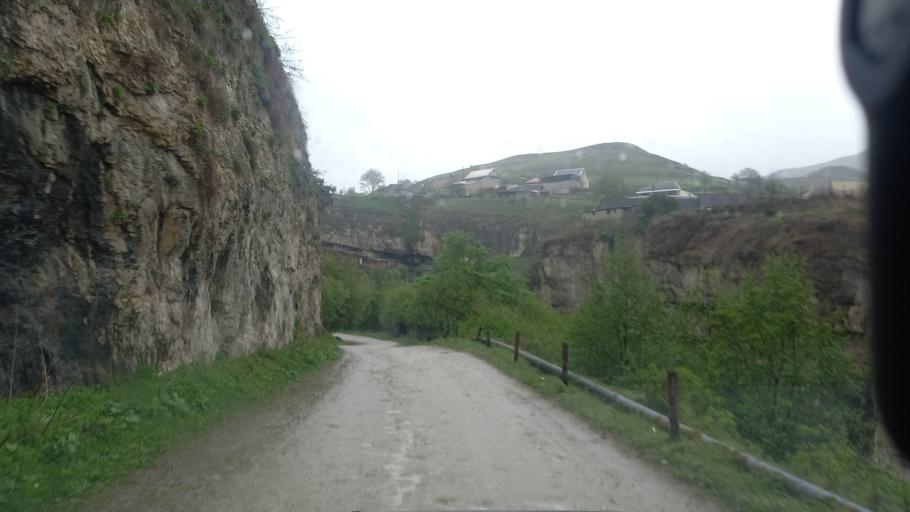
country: RU
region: Kabardino-Balkariya
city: Gundelen
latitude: 43.5969
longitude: 43.1504
